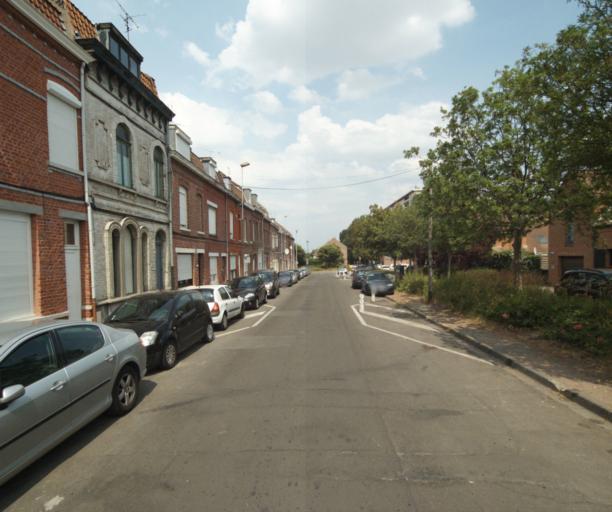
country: FR
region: Nord-Pas-de-Calais
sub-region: Departement du Nord
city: Tourcoing
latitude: 50.7275
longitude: 3.1467
